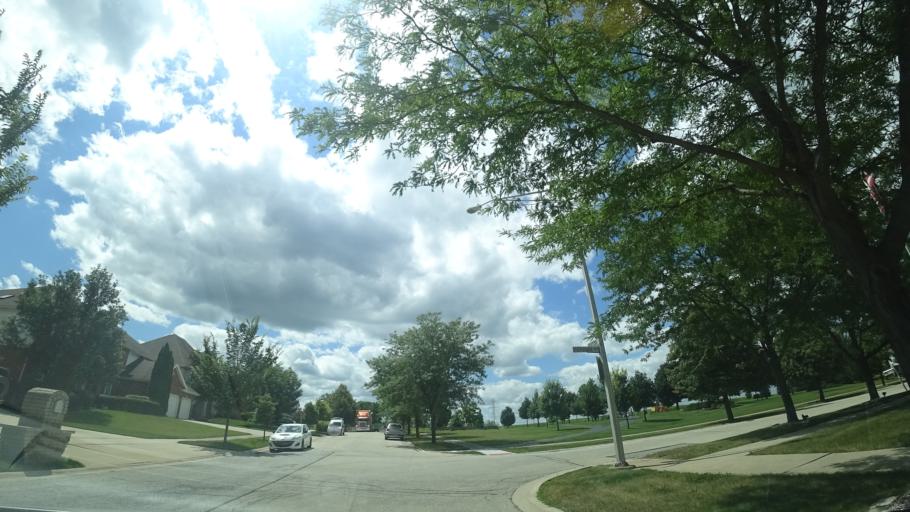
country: US
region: Illinois
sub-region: Will County
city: Homer Glen
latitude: 41.5793
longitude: -87.8960
